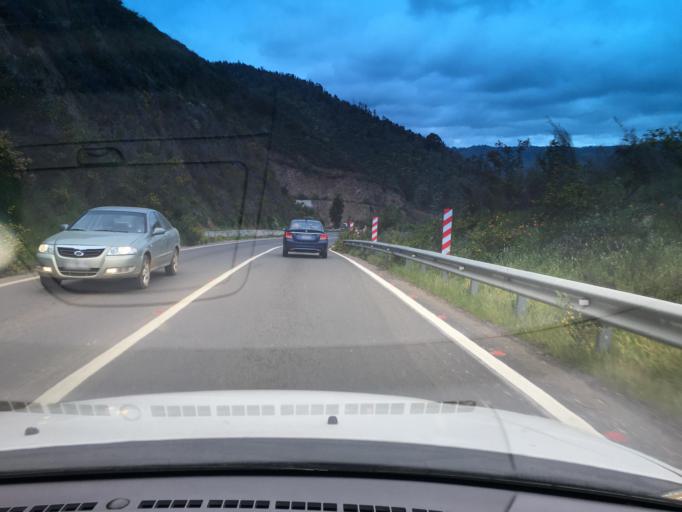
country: CL
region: Valparaiso
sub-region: Provincia de Valparaiso
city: Valparaiso
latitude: -33.0964
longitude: -71.6574
